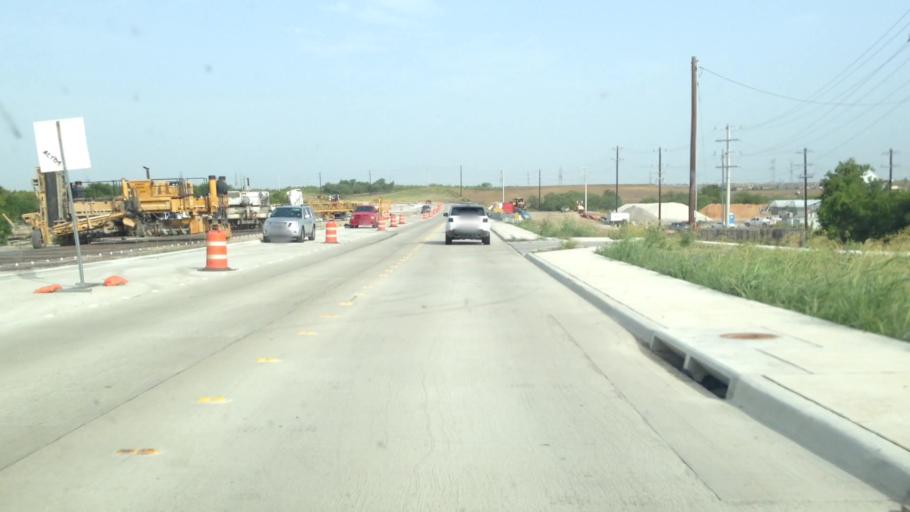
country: US
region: Texas
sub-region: Denton County
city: The Colony
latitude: 33.0456
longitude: -96.8916
